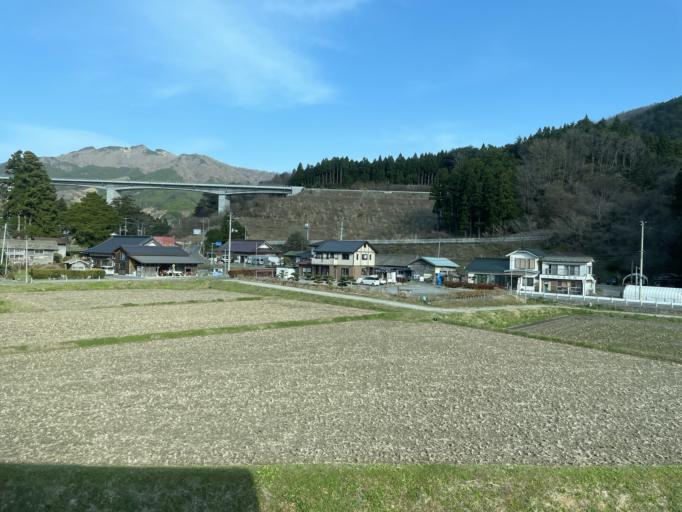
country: JP
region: Iwate
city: Ofunato
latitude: 39.1433
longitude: 141.8257
